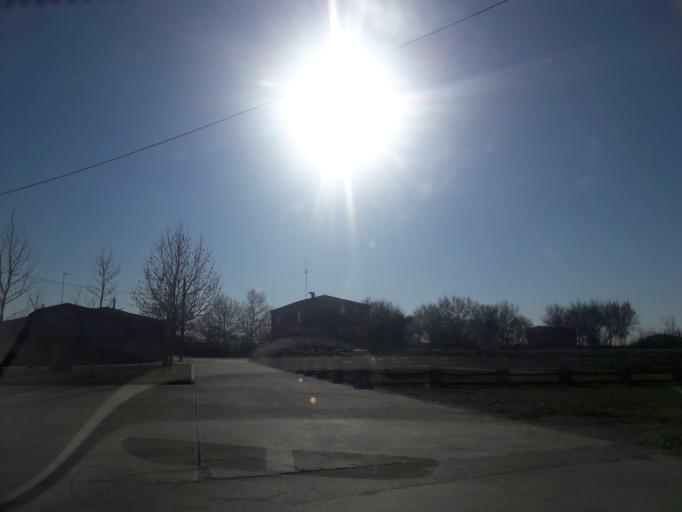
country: ES
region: Castille and Leon
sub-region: Provincia de Salamanca
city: Penarandilla
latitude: 40.8821
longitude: -5.3939
